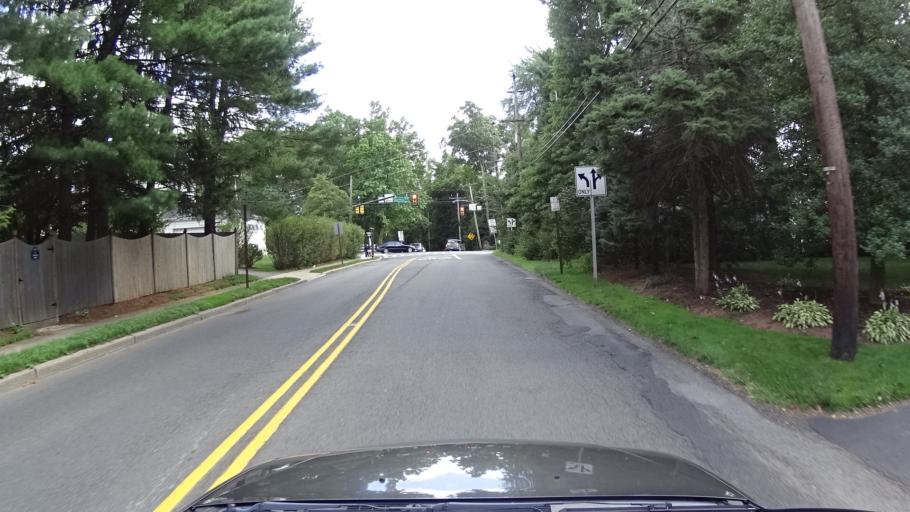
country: US
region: New Jersey
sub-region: Morris County
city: Chatham
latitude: 40.7206
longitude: -74.3844
